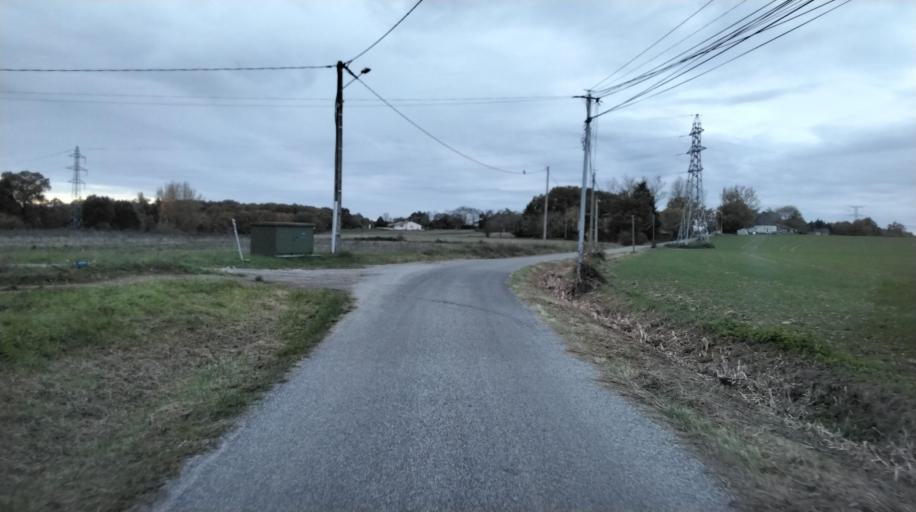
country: FR
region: Midi-Pyrenees
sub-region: Departement de la Haute-Garonne
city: Berat
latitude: 43.3905
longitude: 1.2009
